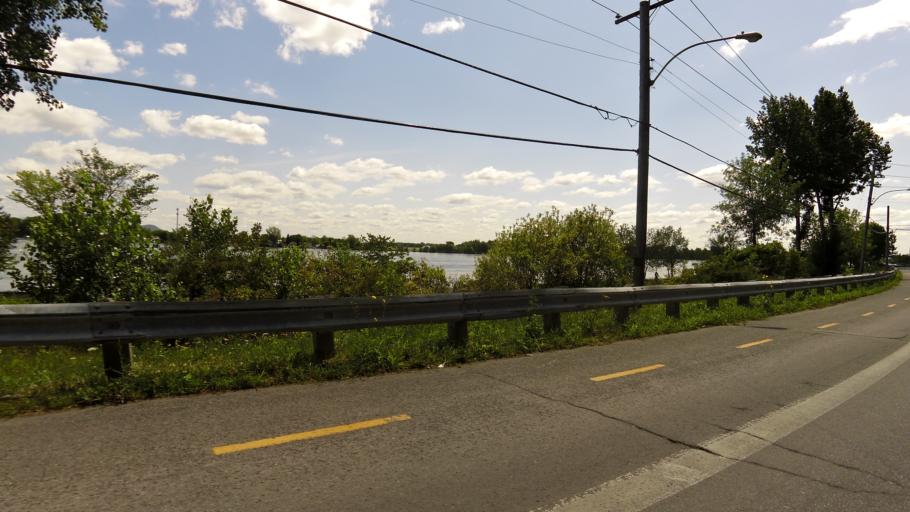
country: CA
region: Quebec
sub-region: Monteregie
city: Saint-Jean-sur-Richelieu
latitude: 45.3398
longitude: -73.2666
